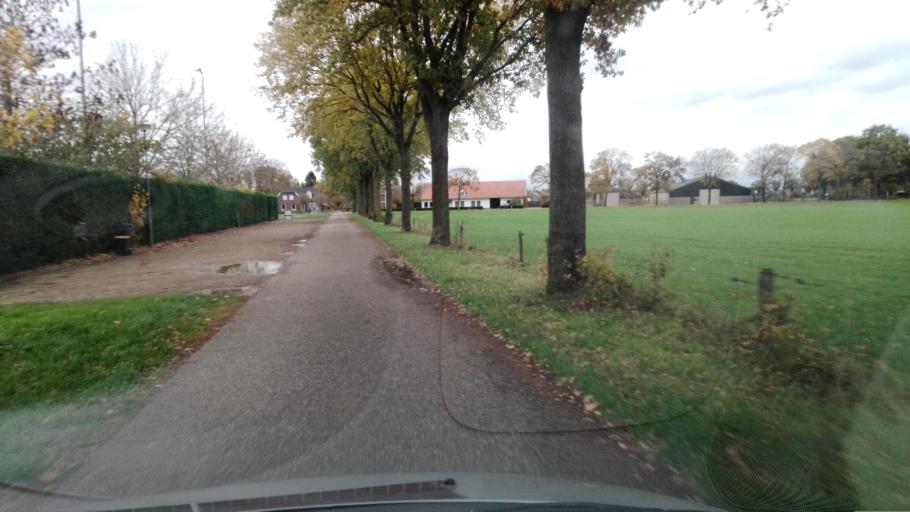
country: NL
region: Limburg
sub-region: Gemeente Beesel
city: Reuver
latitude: 51.2757
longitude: 6.0828
